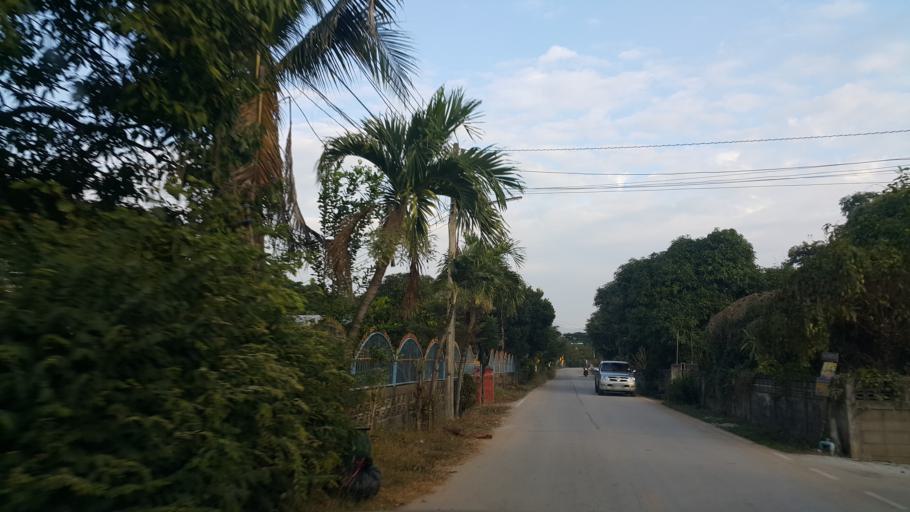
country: TH
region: Lampang
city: Sop Prap
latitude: 17.9013
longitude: 99.3296
